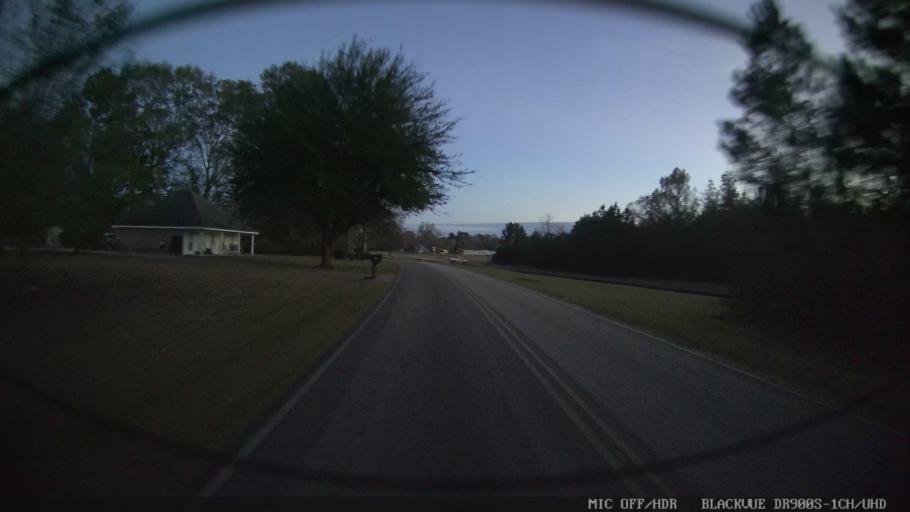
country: US
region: Mississippi
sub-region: Forrest County
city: Hattiesburg
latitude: 31.1689
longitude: -89.2177
